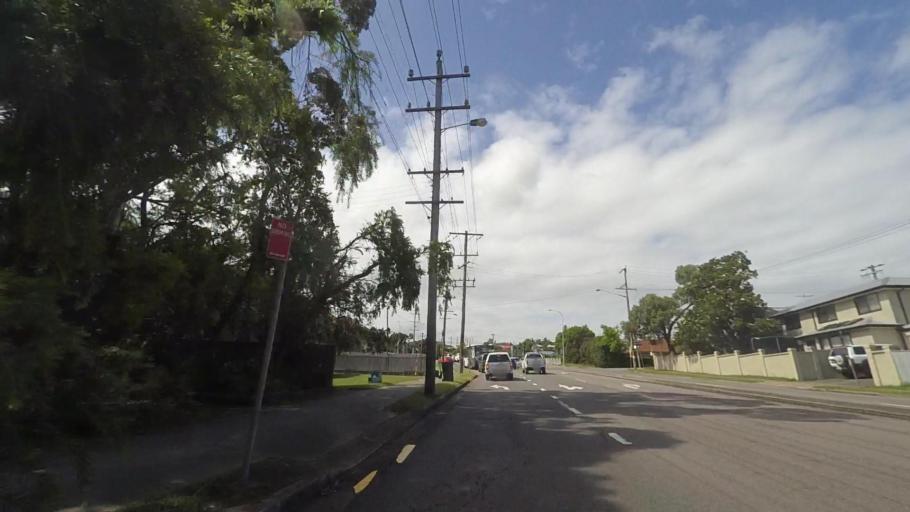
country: AU
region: New South Wales
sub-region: Newcastle
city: North Lambton
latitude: -32.9102
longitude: 151.7051
